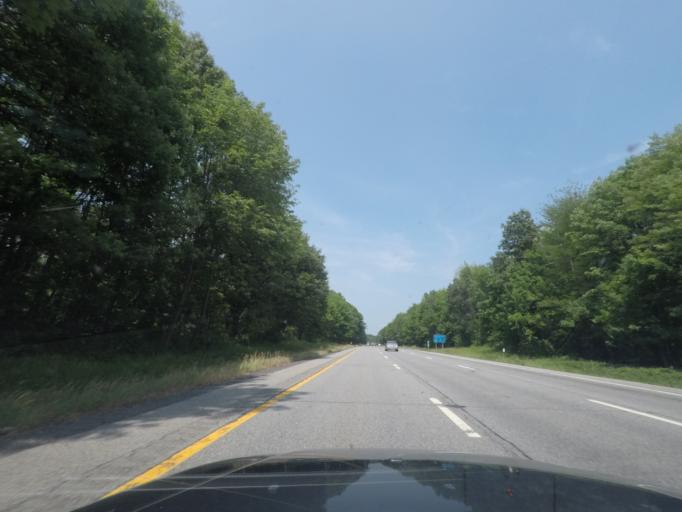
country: US
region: New York
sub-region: Saratoga County
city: Saratoga Springs
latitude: 43.1764
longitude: -73.7092
